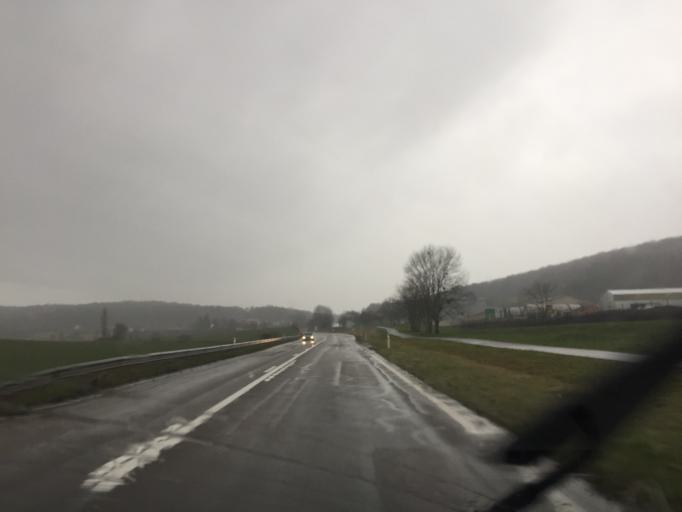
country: FR
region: Franche-Comte
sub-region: Departement du Jura
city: Mouchard
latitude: 46.9838
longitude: 5.8164
